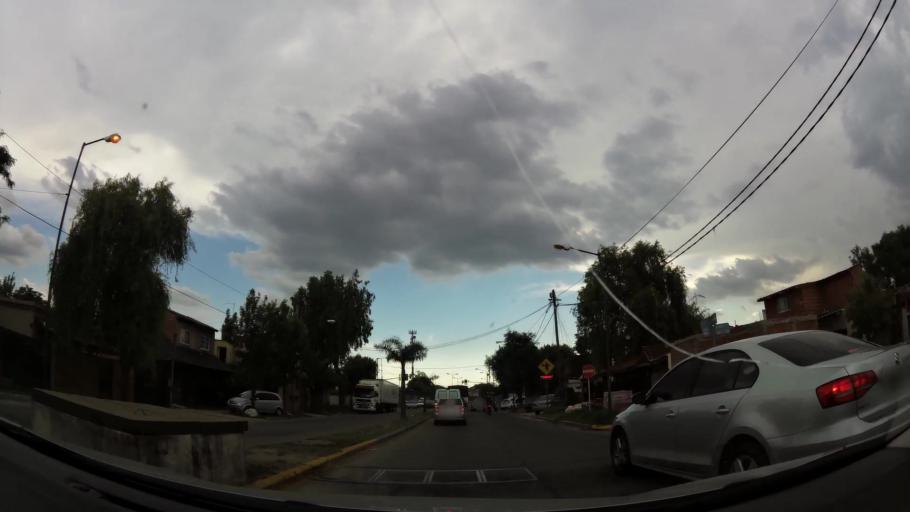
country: AR
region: Buenos Aires
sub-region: Partido de Tigre
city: Tigre
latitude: -34.4789
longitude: -58.5821
